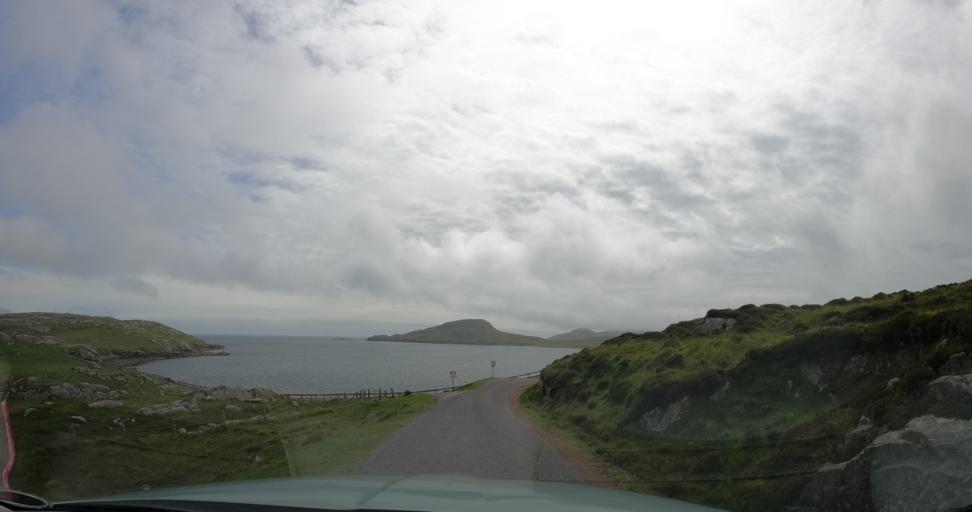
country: GB
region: Scotland
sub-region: Eilean Siar
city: Barra
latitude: 56.9344
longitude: -7.5188
